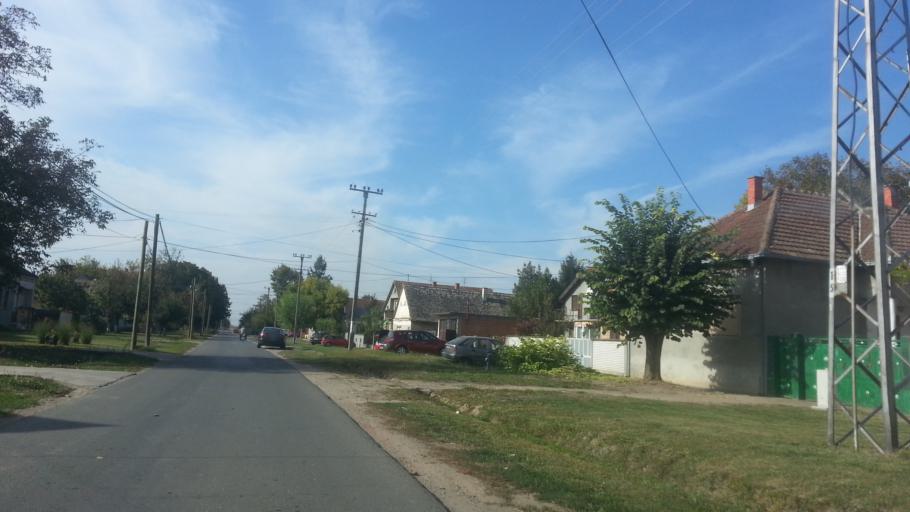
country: RS
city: Belegis
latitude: 45.0178
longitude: 20.3201
